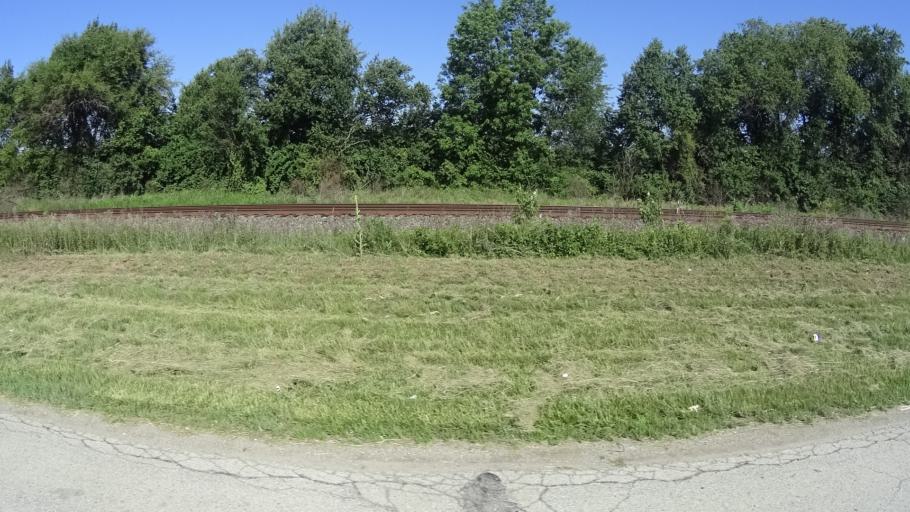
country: US
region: Indiana
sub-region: Madison County
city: Pendleton
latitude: 39.9938
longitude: -85.7389
